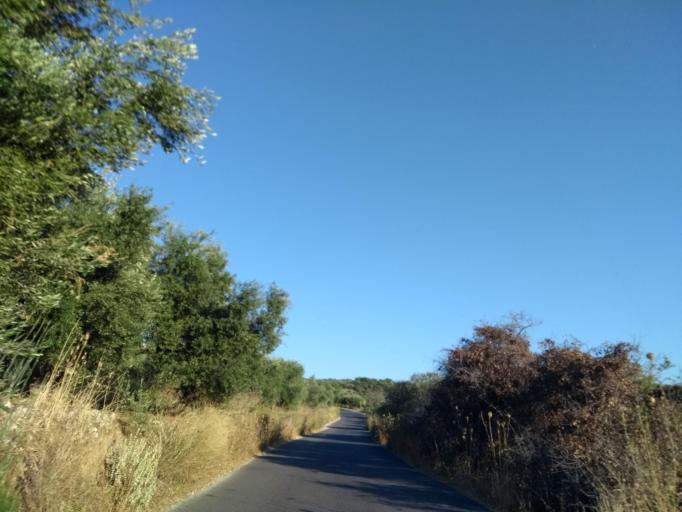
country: GR
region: Crete
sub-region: Nomos Chanias
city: Kalivai
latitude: 35.4377
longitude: 24.1730
